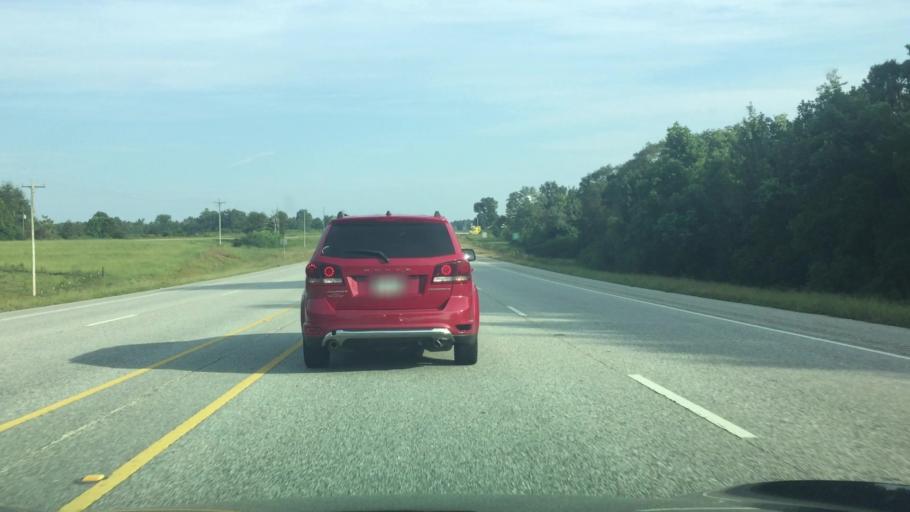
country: US
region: Alabama
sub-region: Butler County
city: Georgiana
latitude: 31.5234
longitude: -86.7157
